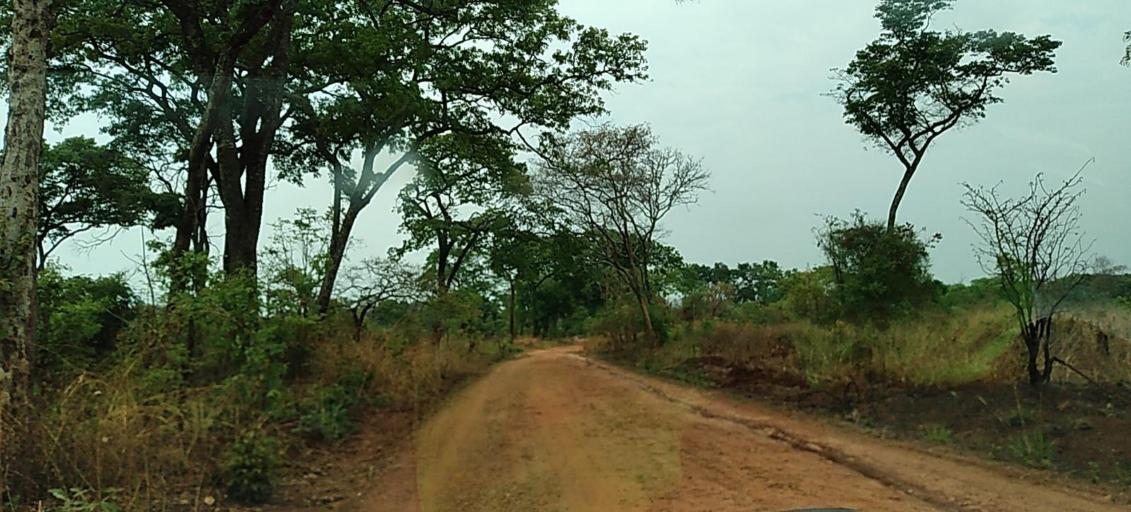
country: ZM
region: North-Western
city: Solwezi
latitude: -12.3268
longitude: 26.5204
